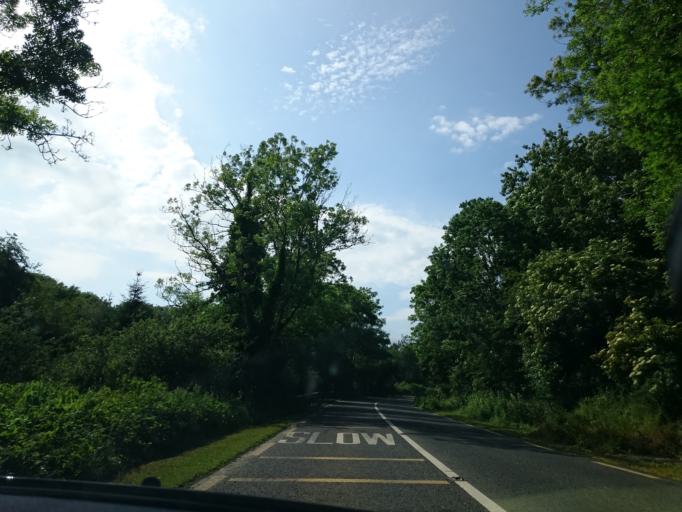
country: IE
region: Leinster
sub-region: Kilkenny
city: Thomastown
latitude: 52.5462
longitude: -7.2302
